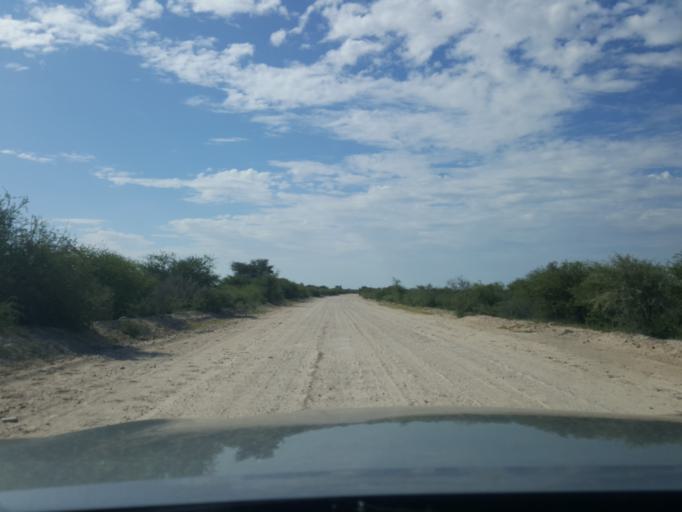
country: BW
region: Kweneng
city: Khudumelapye
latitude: -23.6021
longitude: 24.7231
